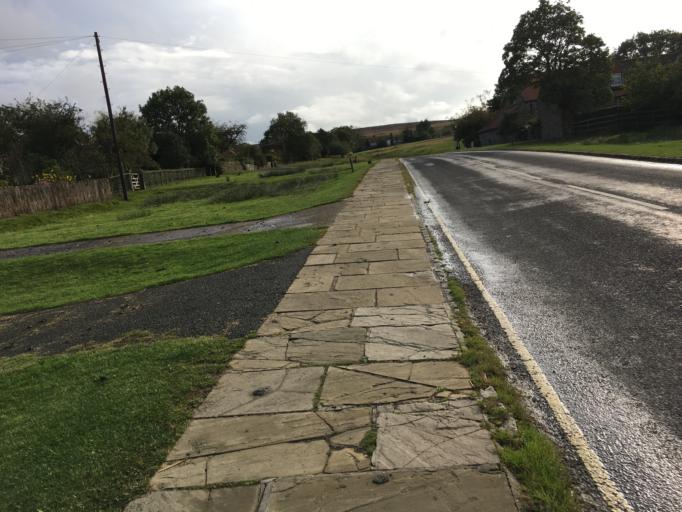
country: GB
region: England
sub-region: North Yorkshire
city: Sleights
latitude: 54.3980
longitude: -0.7224
